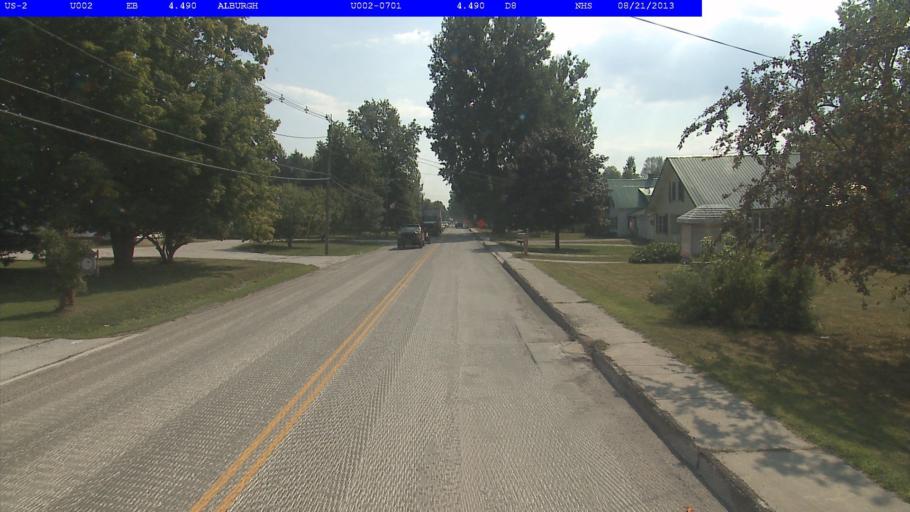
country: US
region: New York
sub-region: Clinton County
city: Rouses Point
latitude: 44.9697
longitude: -73.3026
